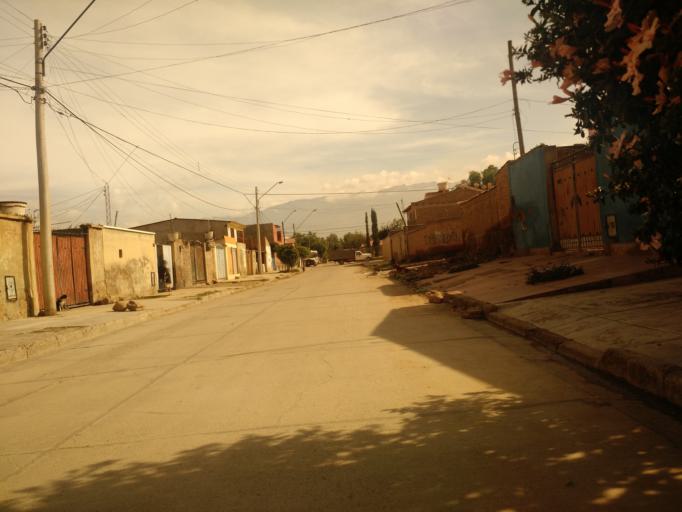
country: BO
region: Cochabamba
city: Cochabamba
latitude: -17.4410
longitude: -66.1568
